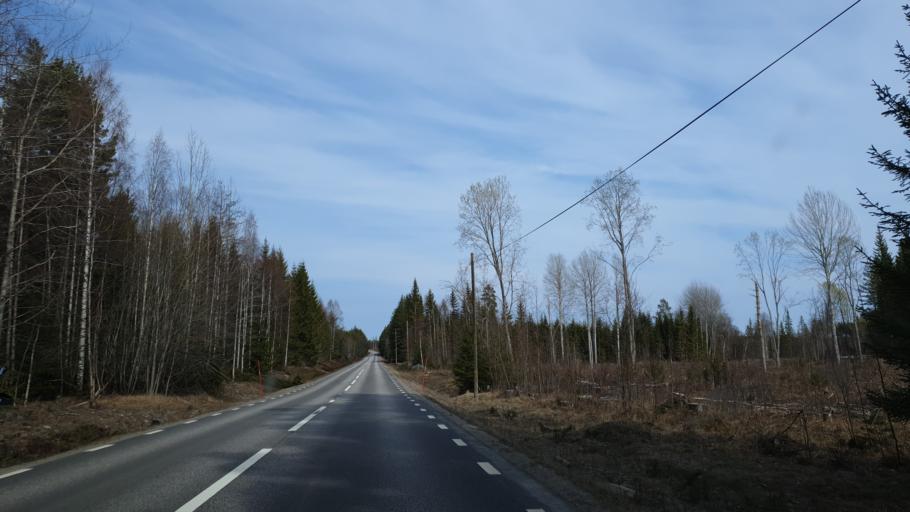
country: SE
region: Gaevleborg
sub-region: Gavle Kommun
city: Norrsundet
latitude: 61.0093
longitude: 17.1337
